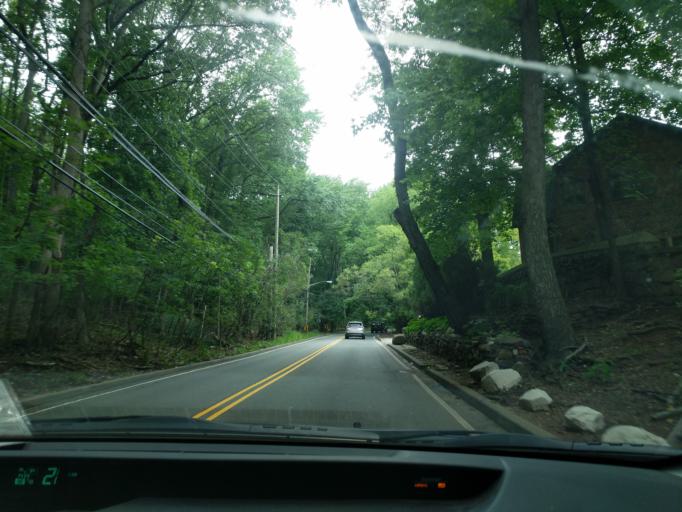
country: US
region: New York
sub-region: Richmond County
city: Staten Island
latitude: 40.5964
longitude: -74.1110
